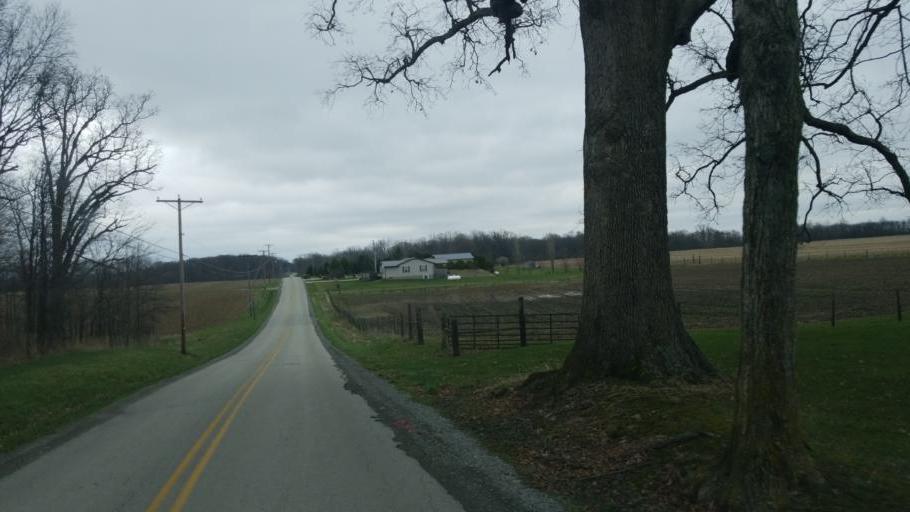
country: US
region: Ohio
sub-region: Wyandot County
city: Upper Sandusky
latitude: 40.7890
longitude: -83.2741
